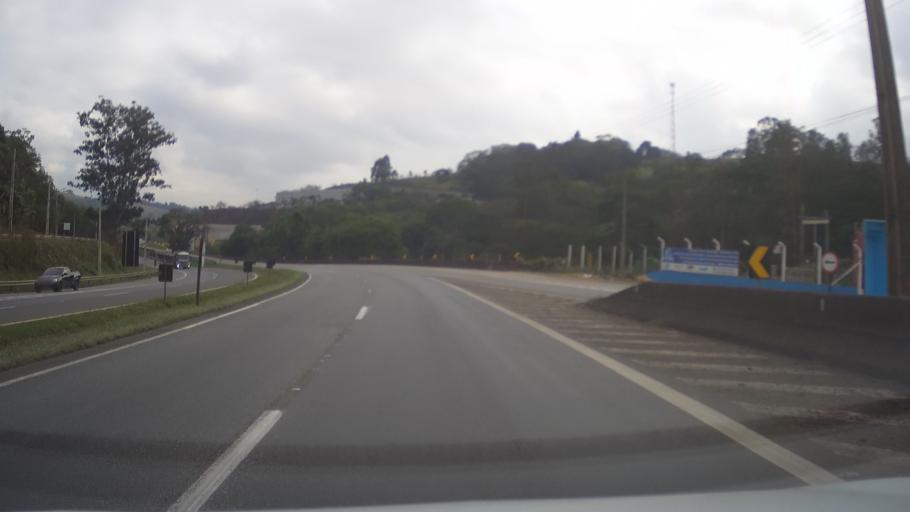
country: BR
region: Minas Gerais
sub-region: Extrema
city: Extrema
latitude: -22.8307
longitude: -46.3156
